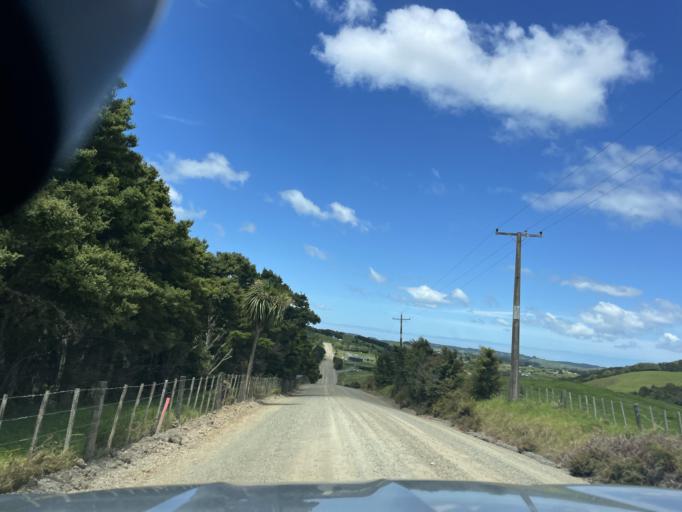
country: NZ
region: Auckland
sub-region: Auckland
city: Wellsford
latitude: -36.1556
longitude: 174.2872
